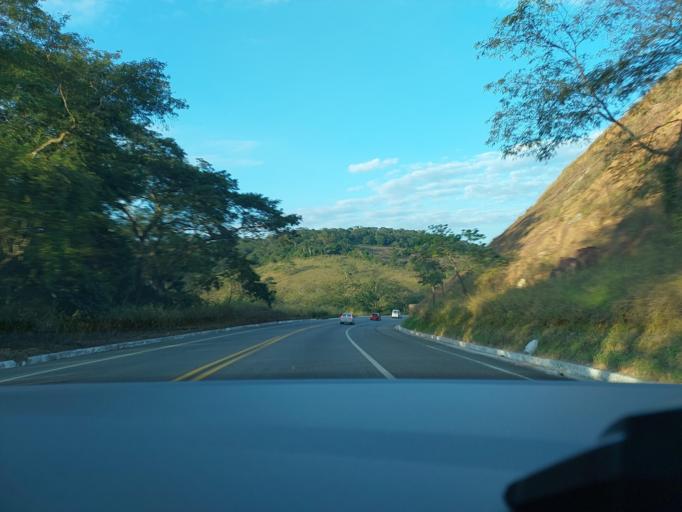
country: BR
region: Minas Gerais
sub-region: Muriae
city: Muriae
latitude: -21.1215
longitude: -42.2131
